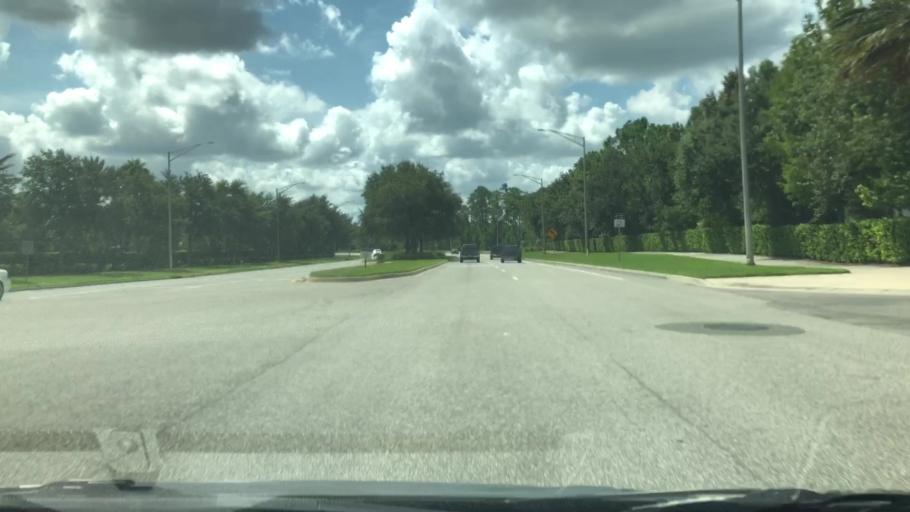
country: US
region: Florida
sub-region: Saint Johns County
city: Fruit Cove
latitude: 30.1327
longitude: -81.5439
